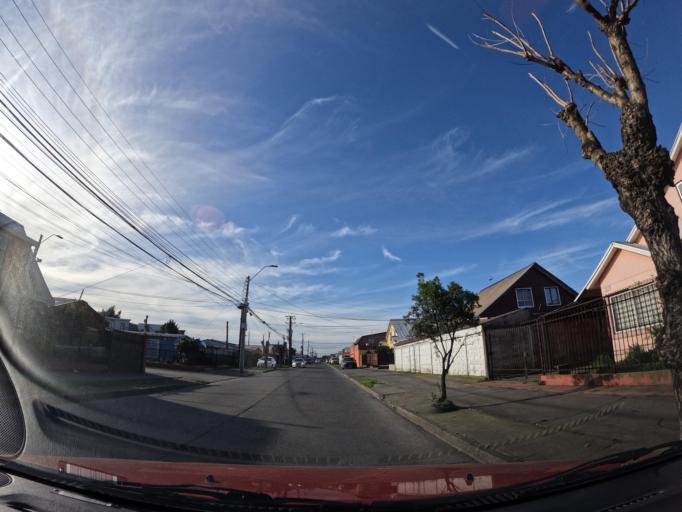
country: CL
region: Biobio
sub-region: Provincia de Concepcion
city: Talcahuano
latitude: -36.7482
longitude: -73.0863
